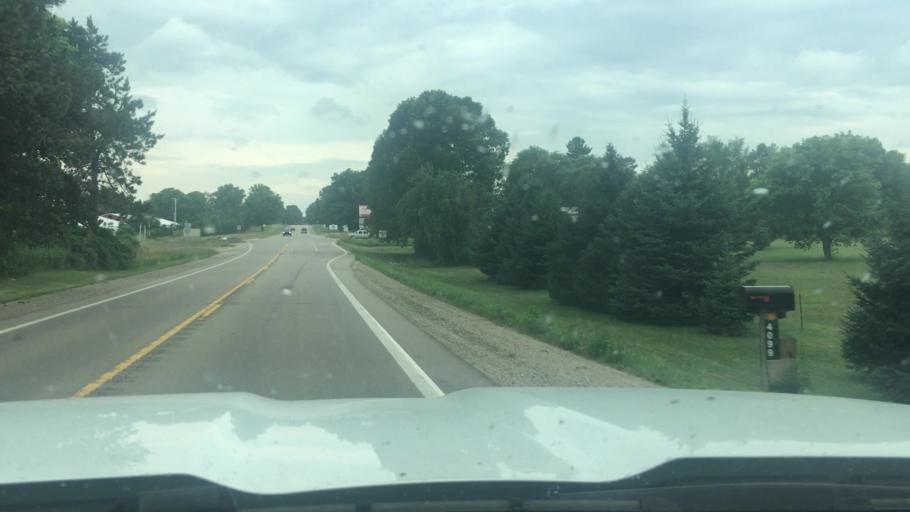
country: US
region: Michigan
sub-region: Ionia County
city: Ionia
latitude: 43.0019
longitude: -84.9932
